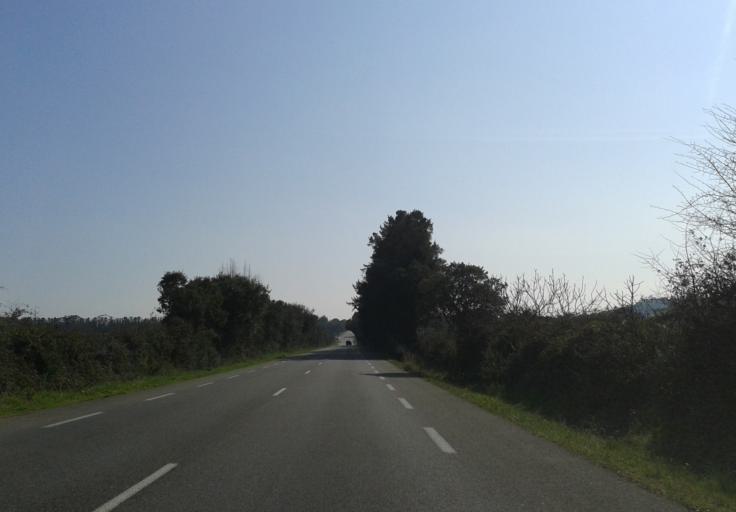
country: FR
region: Corsica
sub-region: Departement de la Haute-Corse
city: Linguizzetta
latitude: 42.2721
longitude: 9.5495
